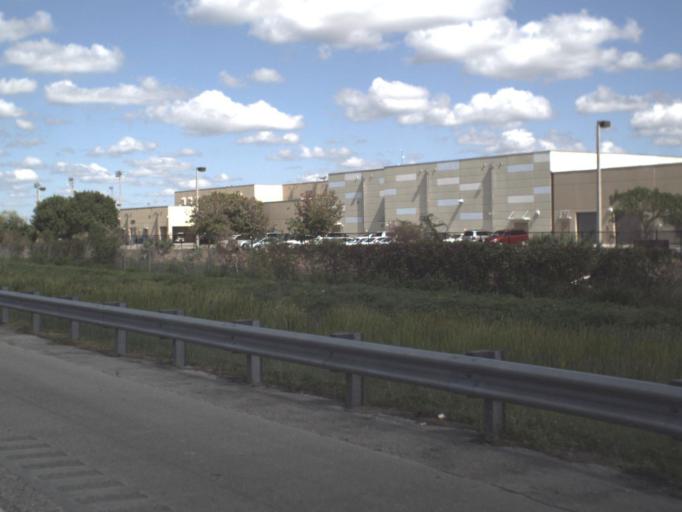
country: US
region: Florida
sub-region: Broward County
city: Coral Springs
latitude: 26.2624
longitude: -80.2969
